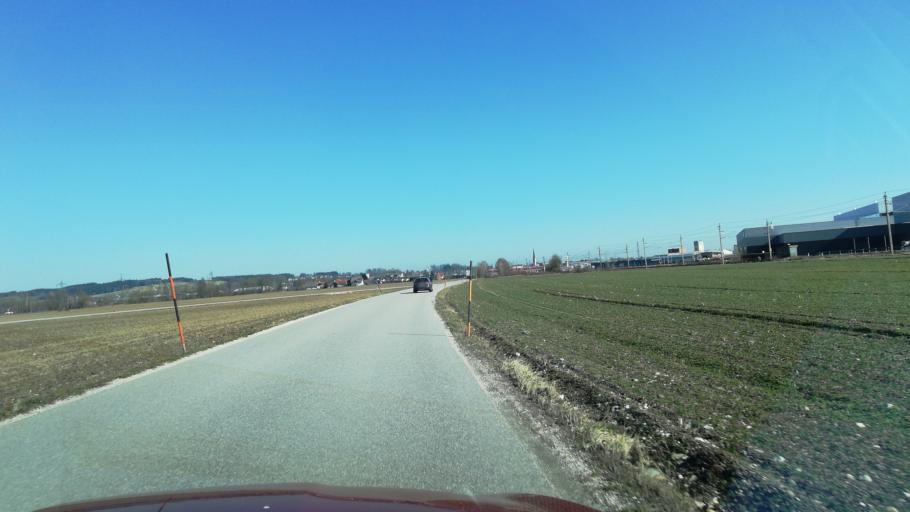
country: AT
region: Upper Austria
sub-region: Politischer Bezirk Vocklabruck
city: Oberndorf bei Schwanenstadt
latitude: 48.0435
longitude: 13.7509
